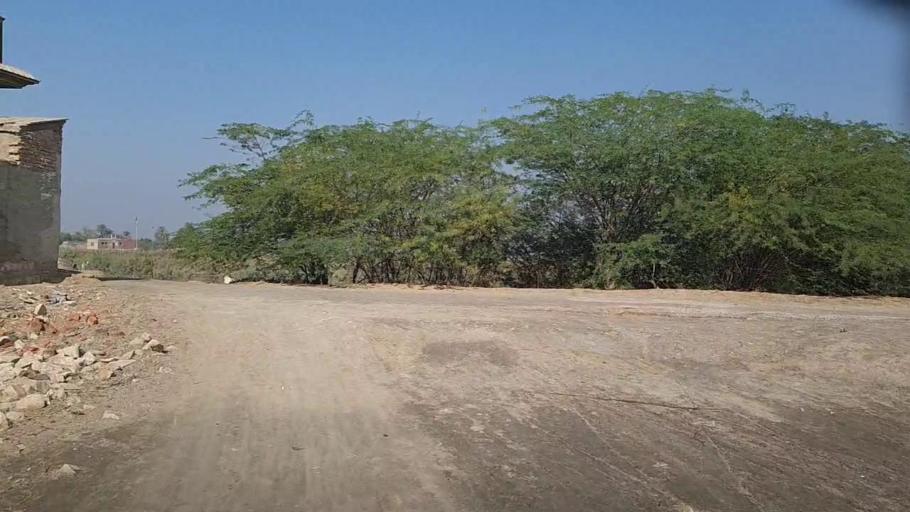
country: PK
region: Sindh
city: Bozdar
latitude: 27.2536
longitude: 68.5977
